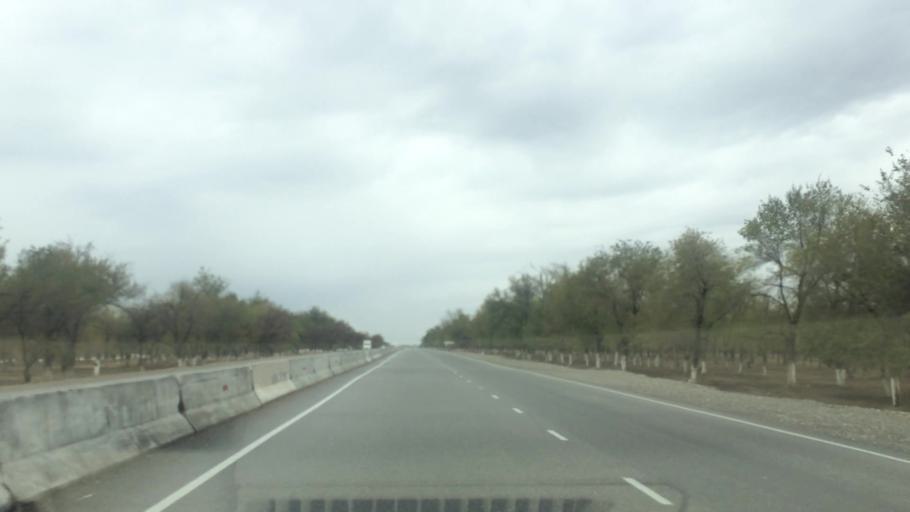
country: UZ
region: Samarqand
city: Bulung'ur
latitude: 39.9171
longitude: 67.5139
